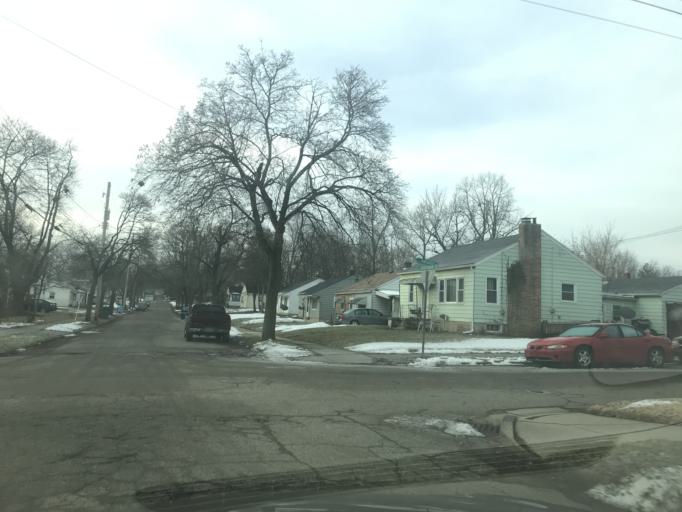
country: US
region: Michigan
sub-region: Ingham County
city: Lansing
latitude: 42.7502
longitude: -84.5702
